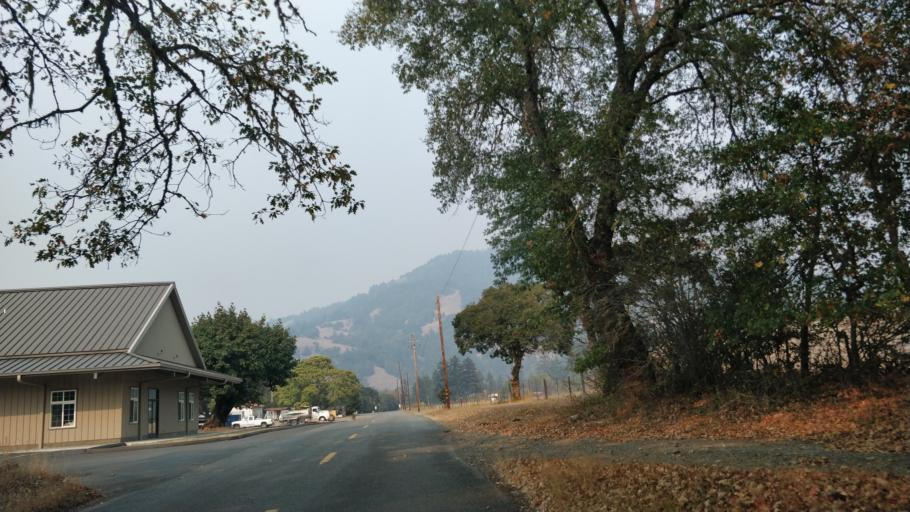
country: US
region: California
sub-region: Humboldt County
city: Rio Dell
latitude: 40.2387
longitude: -124.1323
